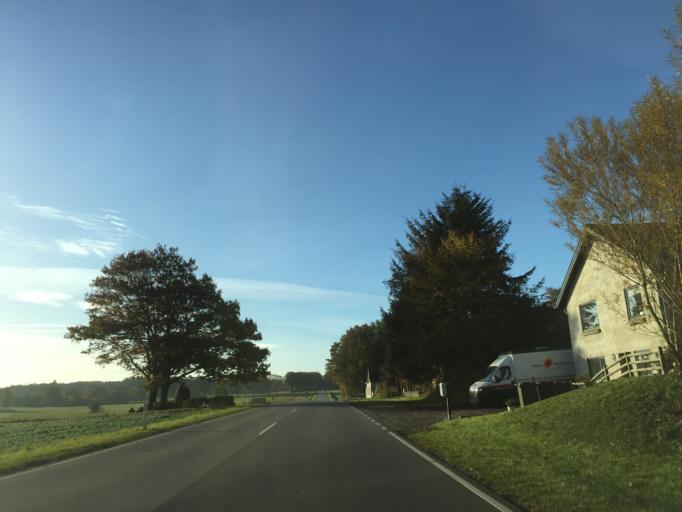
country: DK
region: Central Jutland
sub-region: Skanderborg Kommune
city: Skanderborg
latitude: 56.0884
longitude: 9.8988
